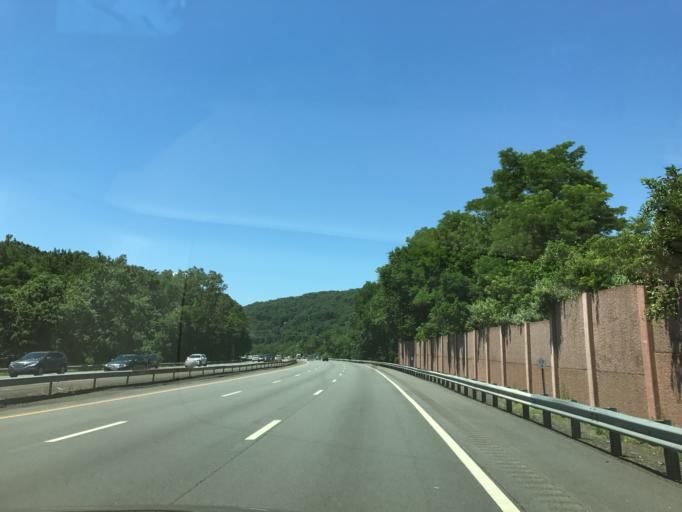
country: US
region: New York
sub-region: Rockland County
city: Suffern
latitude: 41.1216
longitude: -74.1357
